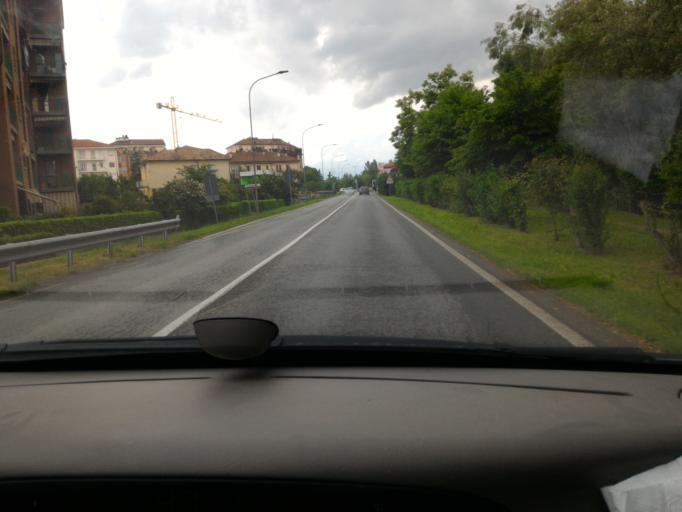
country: IT
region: Piedmont
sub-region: Provincia di Cuneo
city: Savigliano
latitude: 44.6500
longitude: 7.6519
